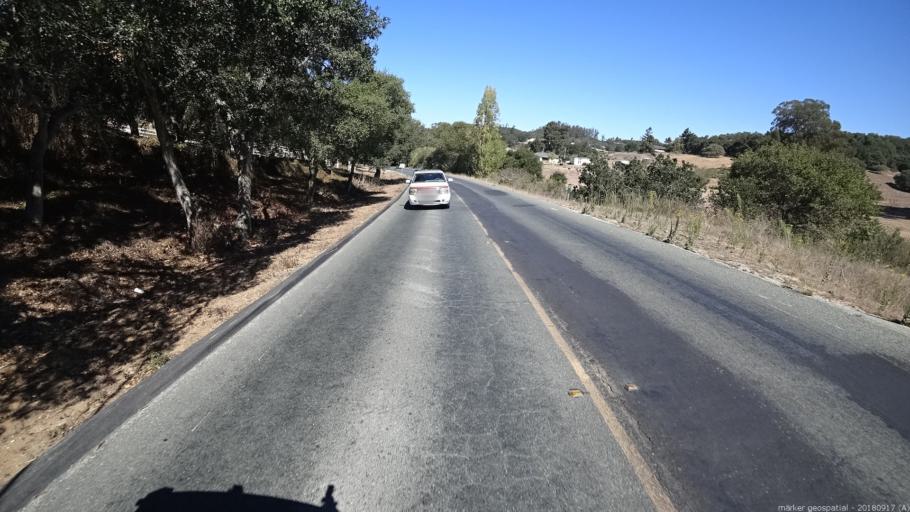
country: US
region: California
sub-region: Monterey County
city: Prunedale
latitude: 36.8126
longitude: -121.6247
